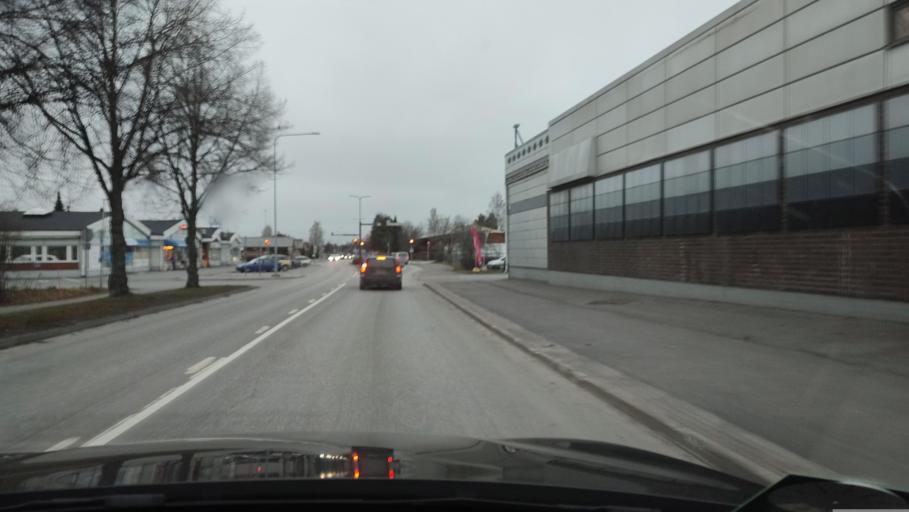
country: FI
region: Southern Ostrobothnia
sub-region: Suupohja
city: Kauhajoki
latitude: 62.4265
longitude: 22.1778
